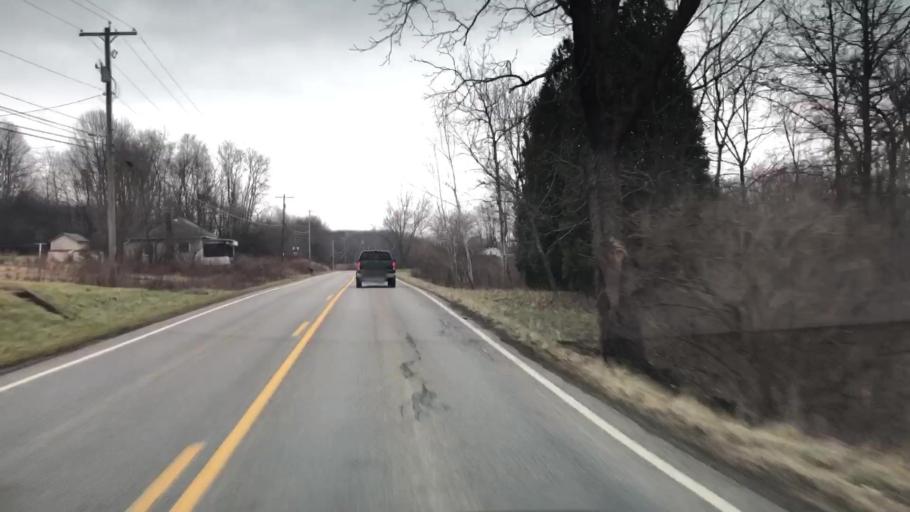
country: US
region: Pennsylvania
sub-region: Mercer County
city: Grove City
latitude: 41.1386
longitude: -80.1401
